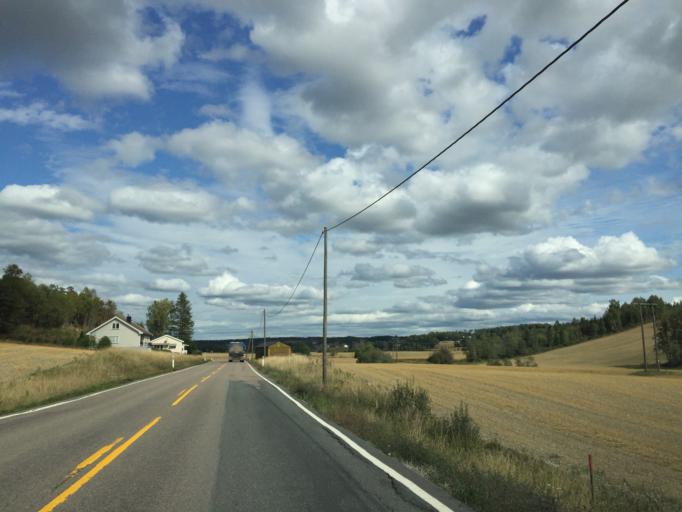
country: NO
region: Ostfold
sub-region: Hobol
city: Elvestad
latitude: 59.6119
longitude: 10.9291
